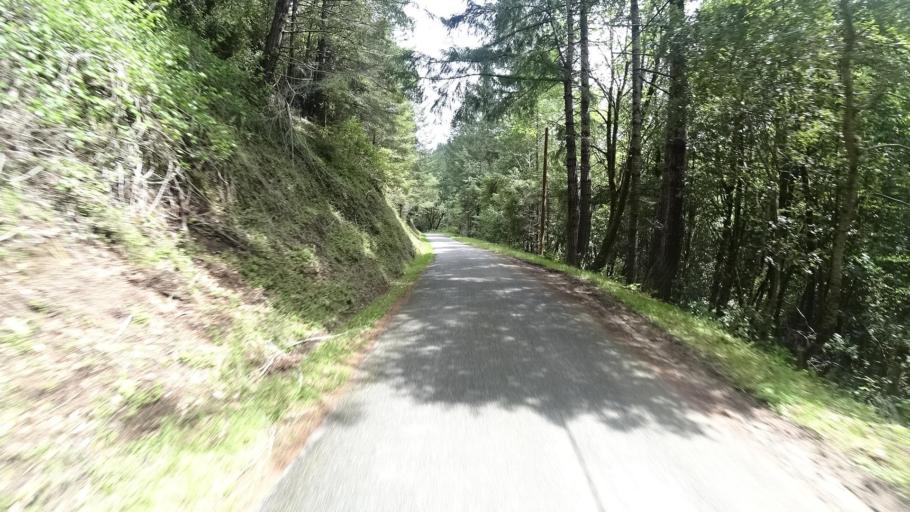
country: US
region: California
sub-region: Humboldt County
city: Blue Lake
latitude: 40.7603
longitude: -123.9133
